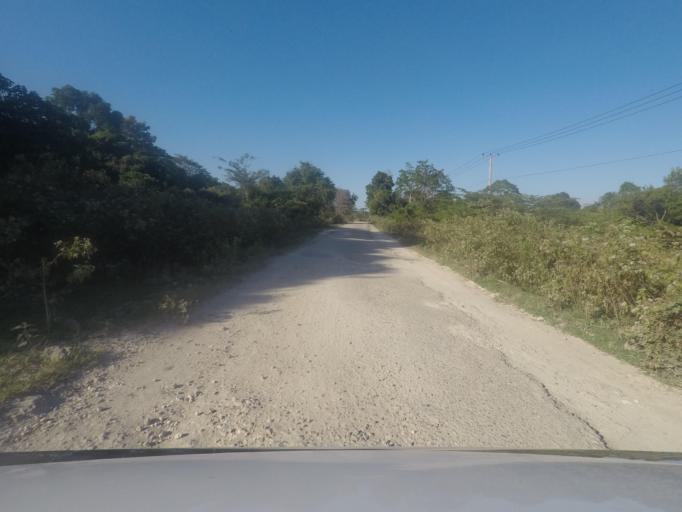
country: TL
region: Lautem
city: Lospalos
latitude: -8.4086
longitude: 127.1692
